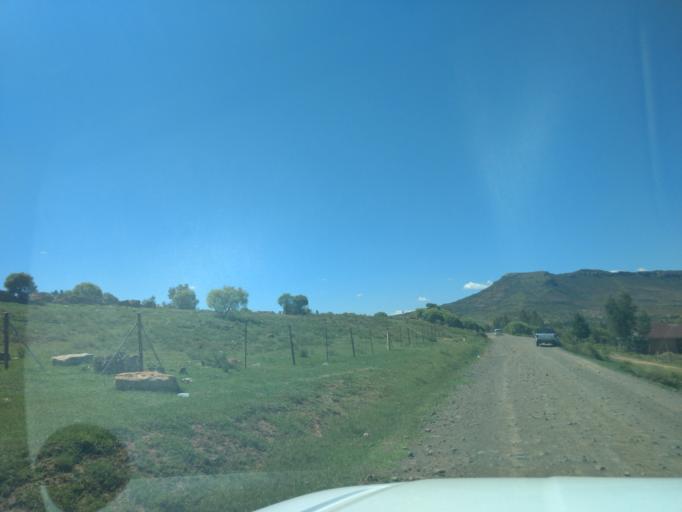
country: LS
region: Maseru
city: Maseru
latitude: -29.4897
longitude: 27.3706
